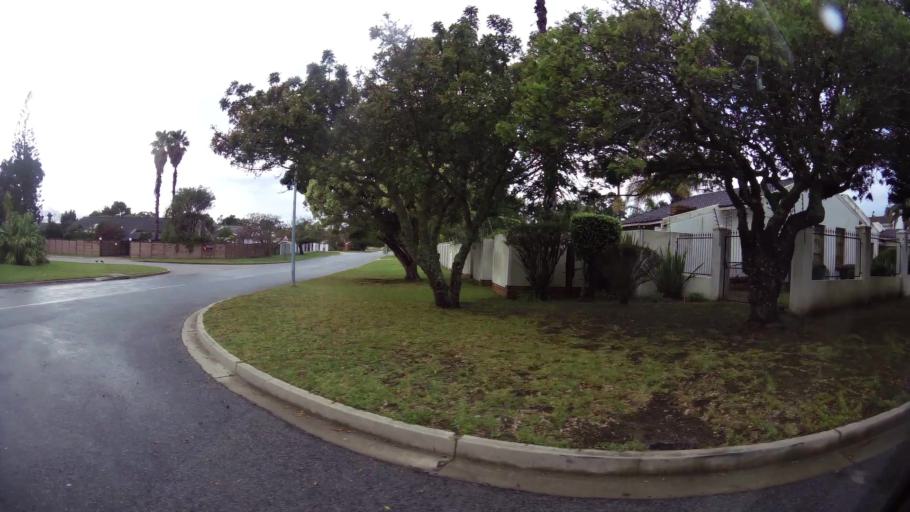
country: ZA
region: Eastern Cape
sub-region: Nelson Mandela Bay Metropolitan Municipality
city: Port Elizabeth
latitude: -33.9945
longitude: 25.5544
